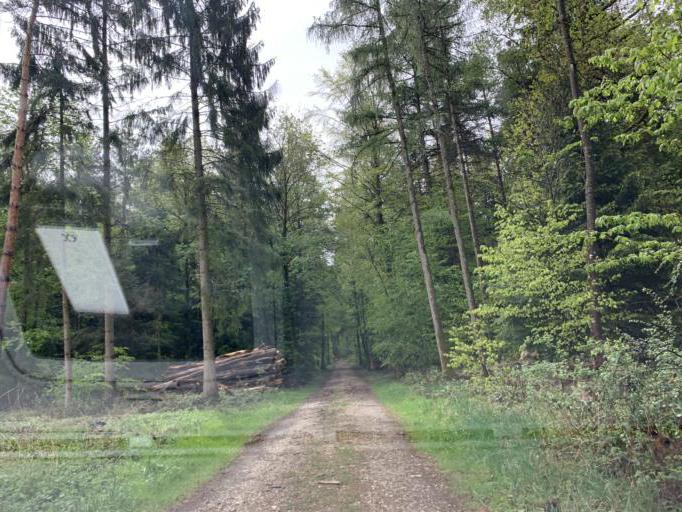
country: CH
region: Schaffhausen
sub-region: Bezirk Schaffhausen
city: Neuhausen
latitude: 47.7018
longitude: 8.6086
